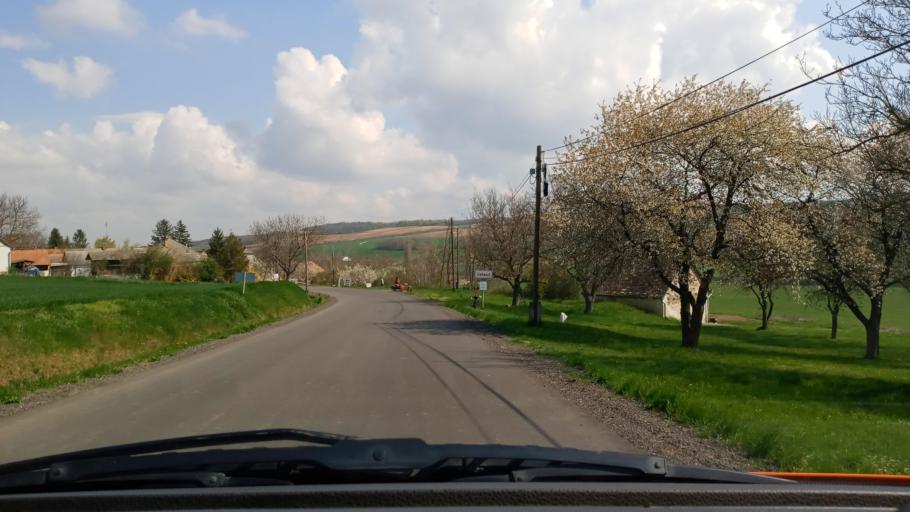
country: HU
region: Baranya
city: Pecsvarad
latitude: 46.0962
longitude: 18.4714
